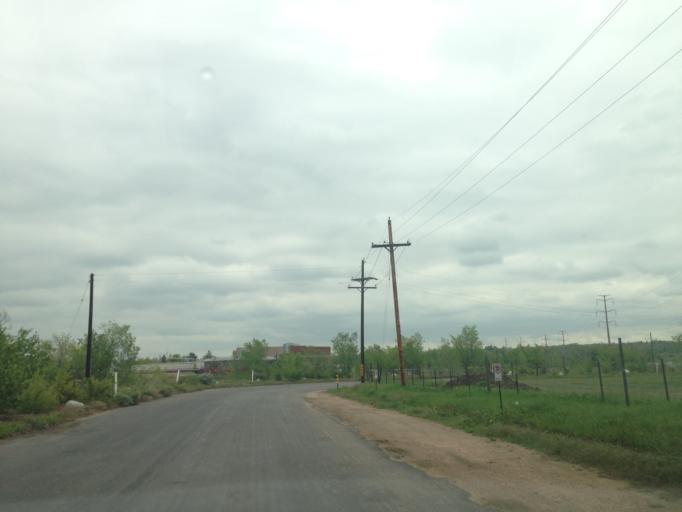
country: US
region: Colorado
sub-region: Boulder County
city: Gunbarrel
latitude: 40.0449
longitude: -105.1833
